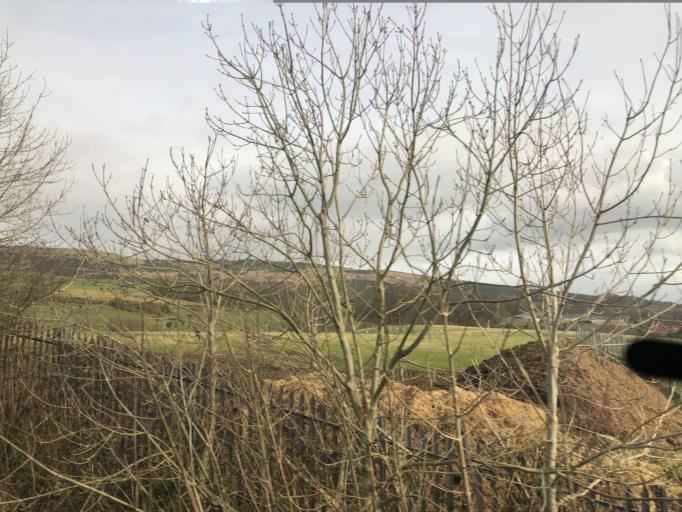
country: GB
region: Scotland
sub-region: Argyll and Bute
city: Helensburgh
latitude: 56.0018
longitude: -4.7100
